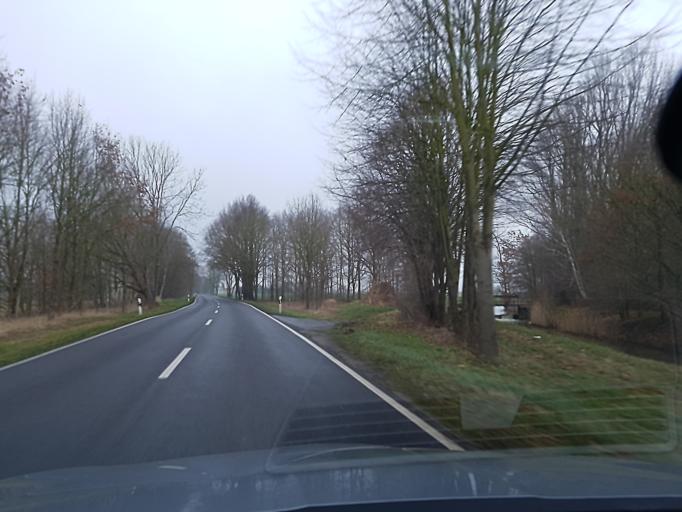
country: DE
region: Brandenburg
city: Doberlug-Kirchhain
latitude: 51.6463
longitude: 13.5569
